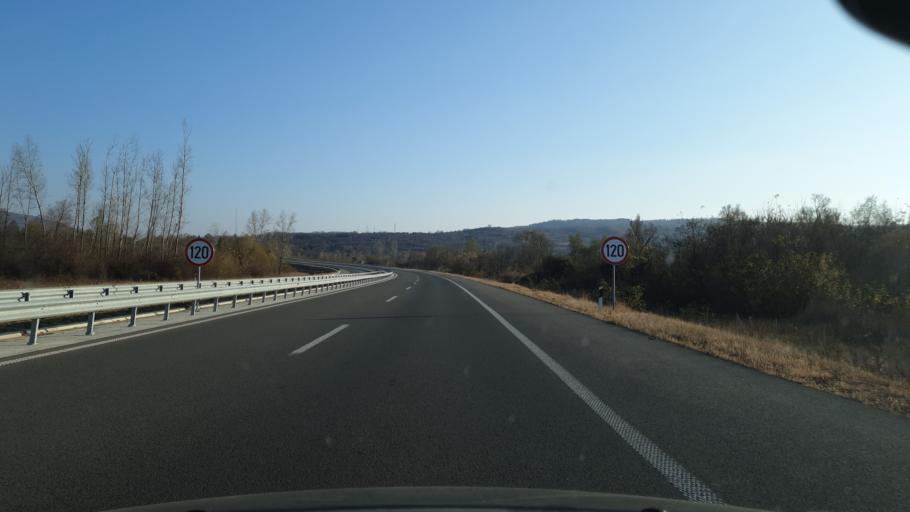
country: RS
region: Central Serbia
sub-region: Pirotski Okrug
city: Dimitrovgrad
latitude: 43.0662
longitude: 22.6792
